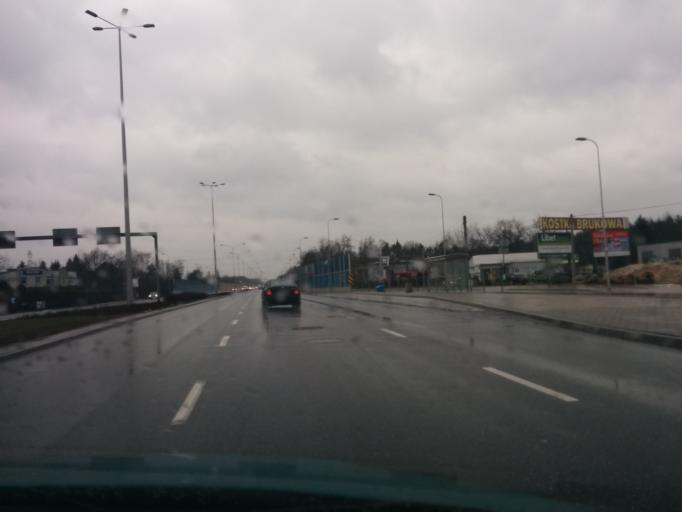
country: PL
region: Masovian Voivodeship
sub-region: Warszawa
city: Bialoleka
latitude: 52.3502
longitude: 20.9461
